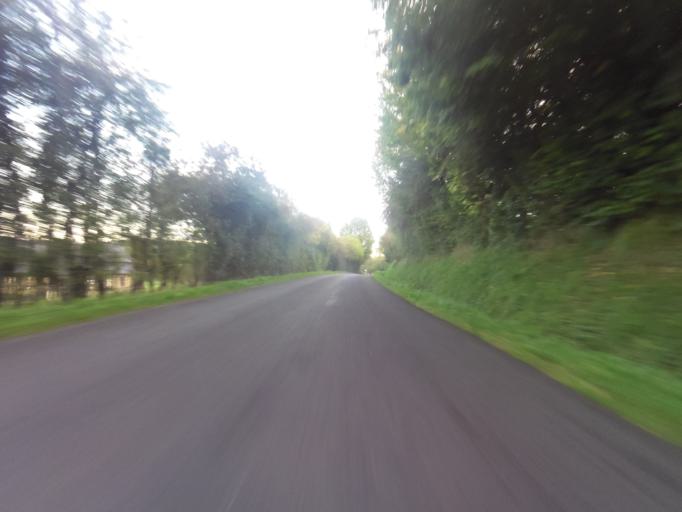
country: FR
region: Lower Normandy
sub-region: Departement de l'Orne
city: Vimoutiers
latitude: 48.9480
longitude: 0.2662
